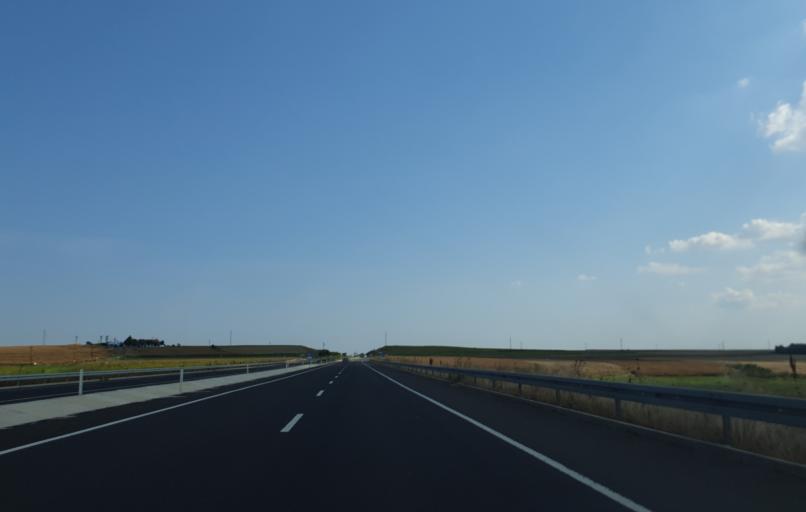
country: TR
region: Tekirdag
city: Muratli
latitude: 41.2153
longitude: 27.5333
